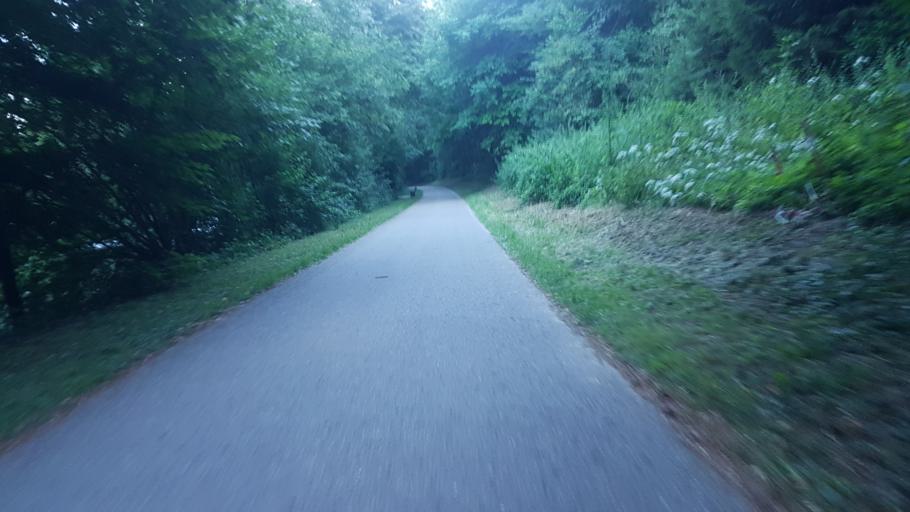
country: DE
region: Baden-Wuerttemberg
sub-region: Regierungsbezirk Stuttgart
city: Neudenau
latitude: 49.2897
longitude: 9.2533
